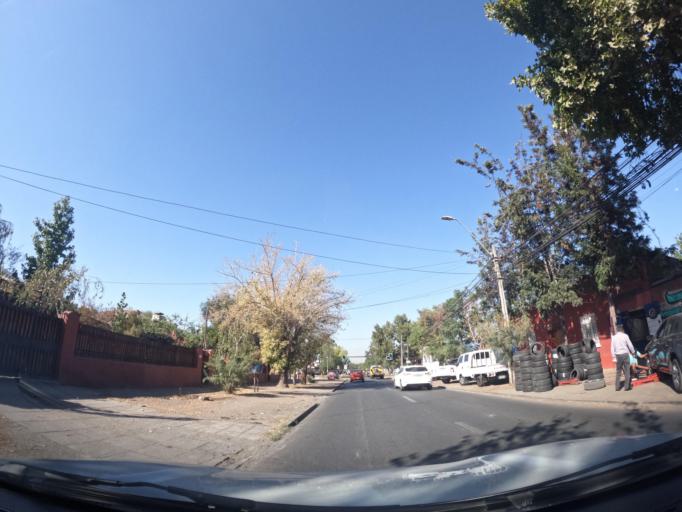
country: CL
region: Santiago Metropolitan
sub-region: Provincia de Santiago
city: Villa Presidente Frei, Nunoa, Santiago, Chile
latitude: -33.4627
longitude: -70.5701
